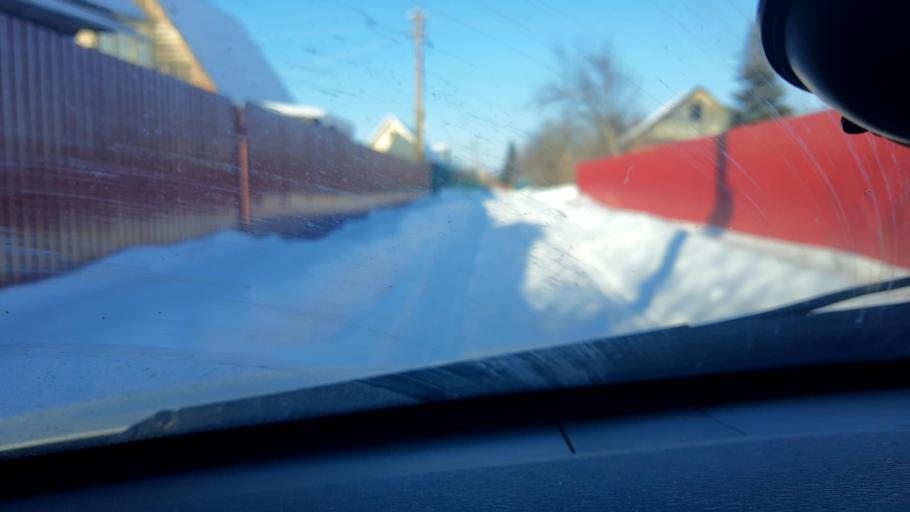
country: RU
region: Bashkortostan
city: Ufa
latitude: 54.5770
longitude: 55.8915
